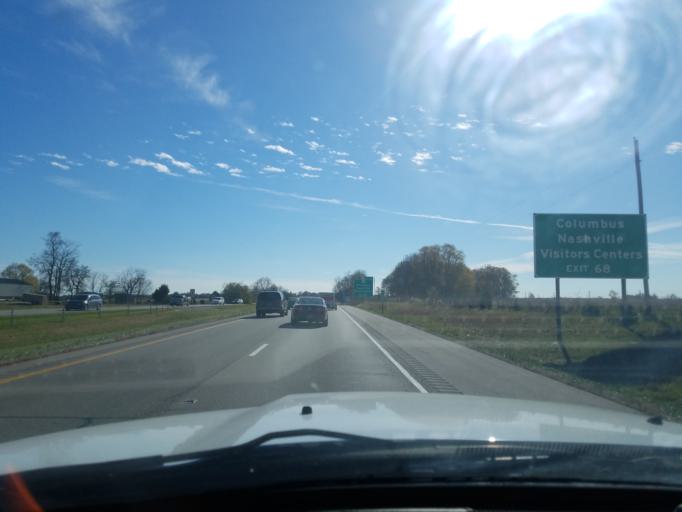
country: US
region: Indiana
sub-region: Bartholomew County
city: Lowell
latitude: 39.2262
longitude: -85.9542
